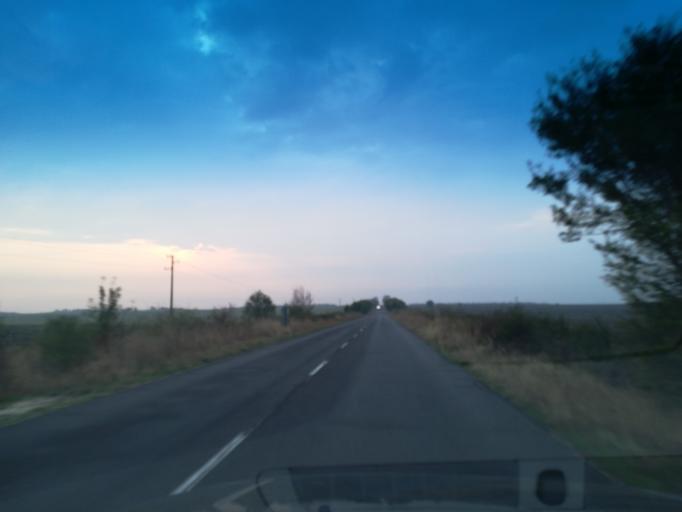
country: BG
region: Stara Zagora
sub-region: Obshtina Chirpan
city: Chirpan
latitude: 42.1806
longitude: 25.2409
